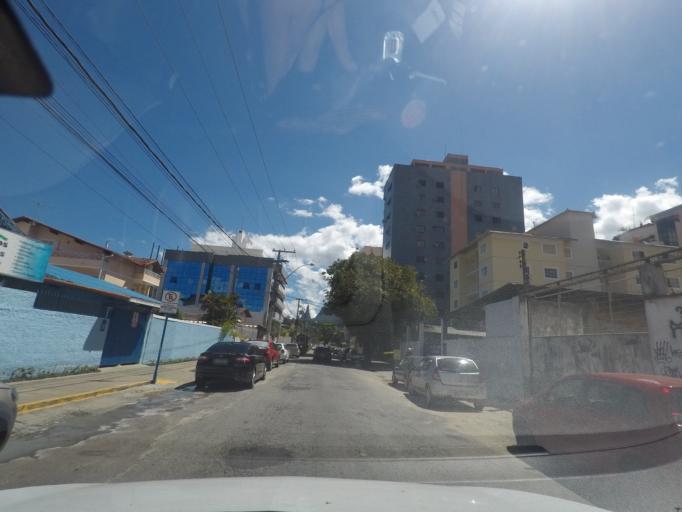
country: BR
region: Rio de Janeiro
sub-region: Teresopolis
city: Teresopolis
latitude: -22.4174
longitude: -42.9715
